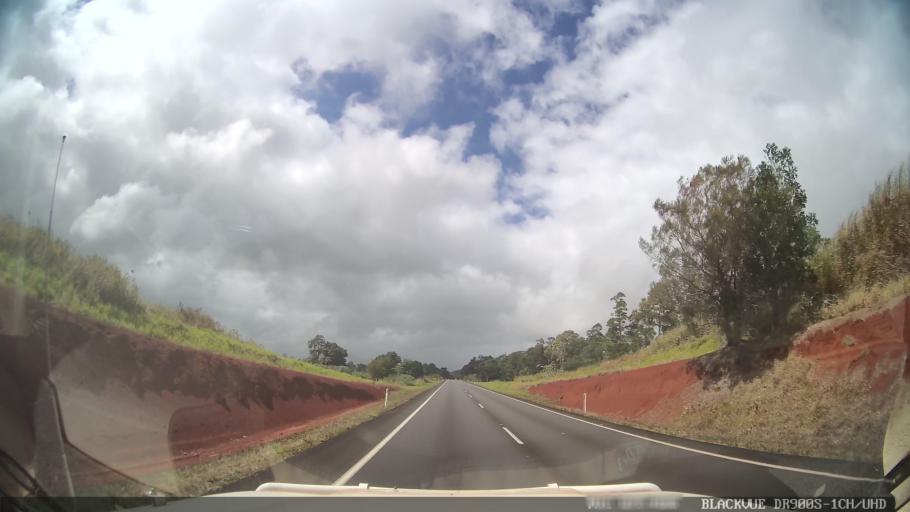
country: AU
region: Queensland
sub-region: Tablelands
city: Atherton
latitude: -17.3022
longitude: 145.6219
